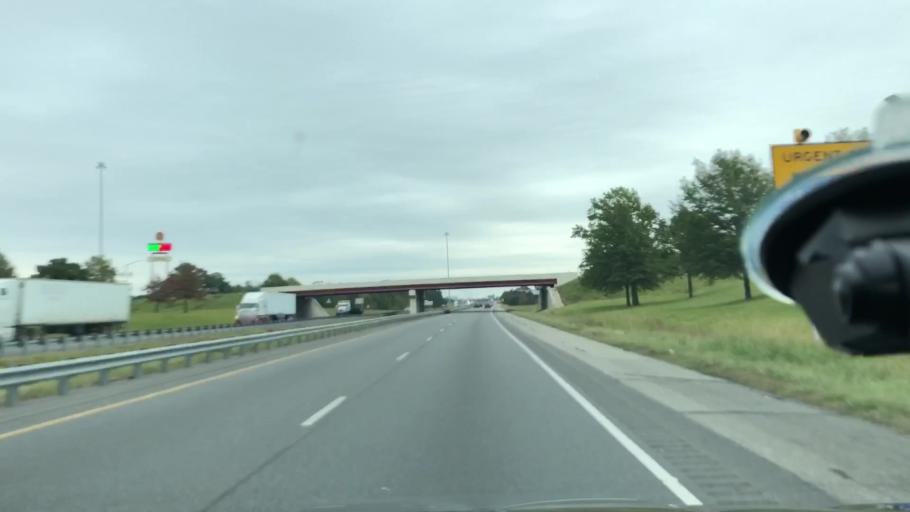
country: US
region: Arkansas
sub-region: Miller County
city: Texarkana
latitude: 33.4754
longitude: -94.0091
